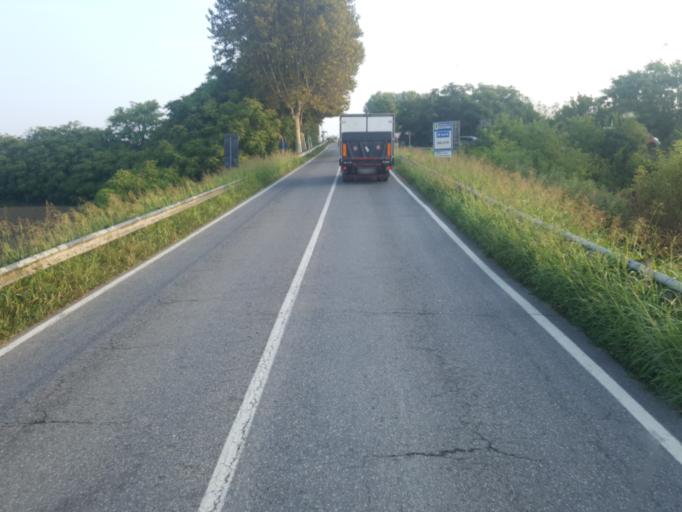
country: IT
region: Emilia-Romagna
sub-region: Provincia di Ferrara
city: San Biagio
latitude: 44.5754
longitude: 11.8743
